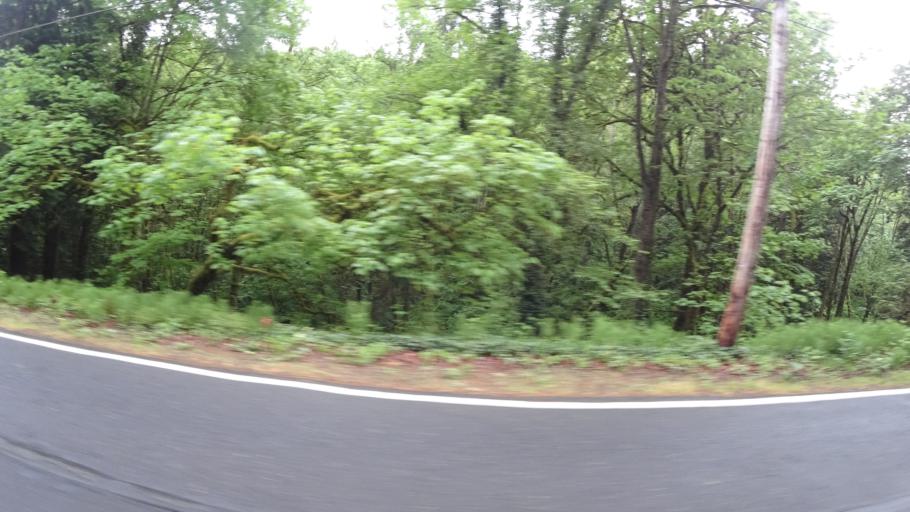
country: US
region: Oregon
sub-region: Washington County
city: West Haven-Sylvan
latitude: 45.5401
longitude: -122.7420
